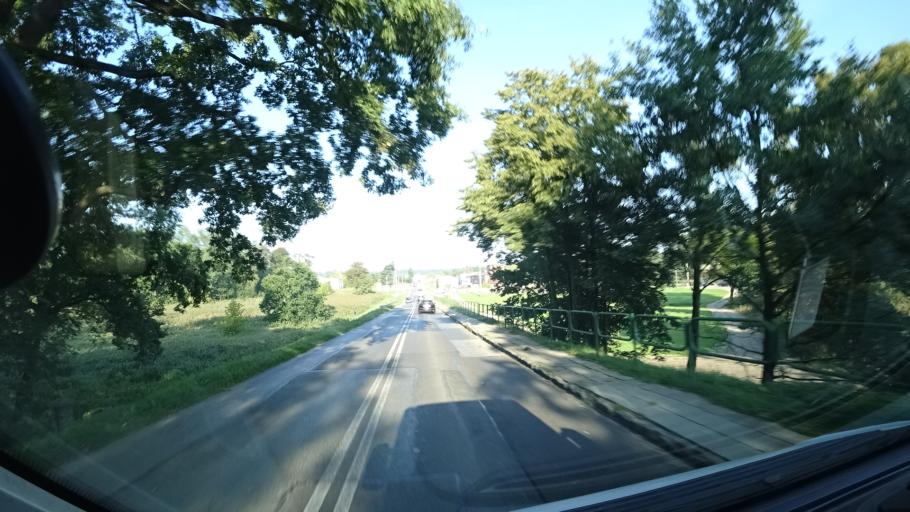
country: PL
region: Silesian Voivodeship
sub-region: Powiat gliwicki
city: Sosnicowice
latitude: 50.2740
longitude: 18.5278
